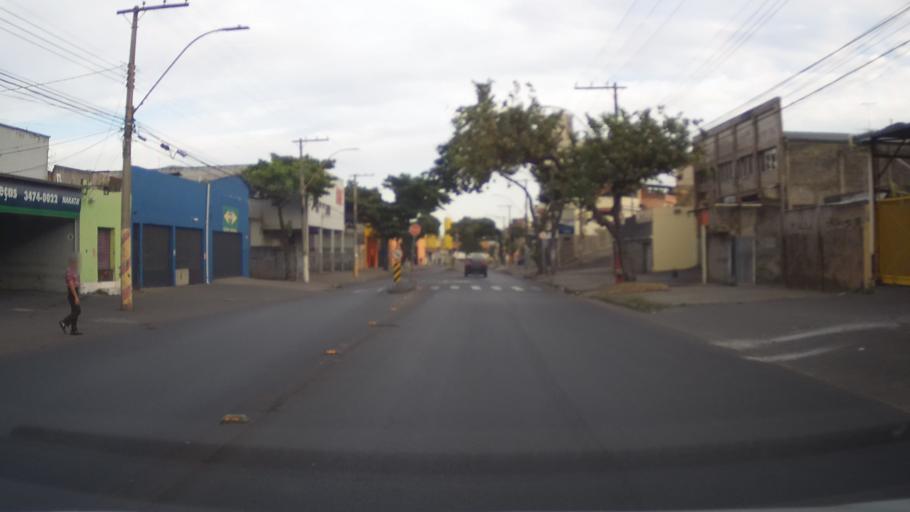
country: BR
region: Minas Gerais
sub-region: Contagem
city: Contagem
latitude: -19.9054
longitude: -44.0058
